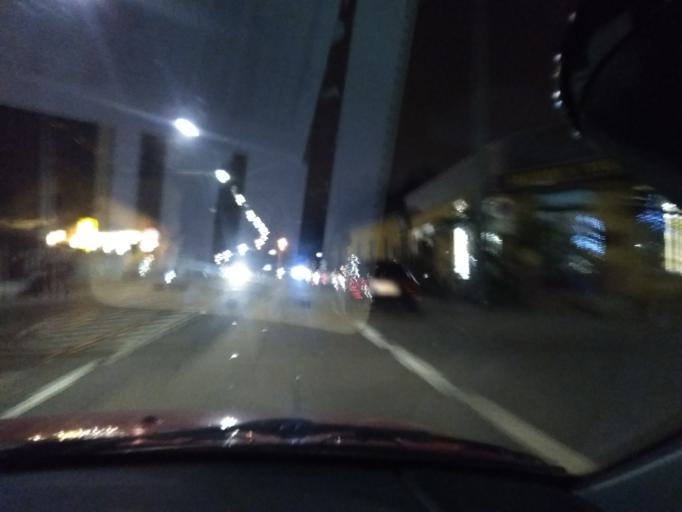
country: AT
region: Lower Austria
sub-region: Politischer Bezirk Modling
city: Perchtoldsdorf
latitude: 48.1551
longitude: 16.2719
